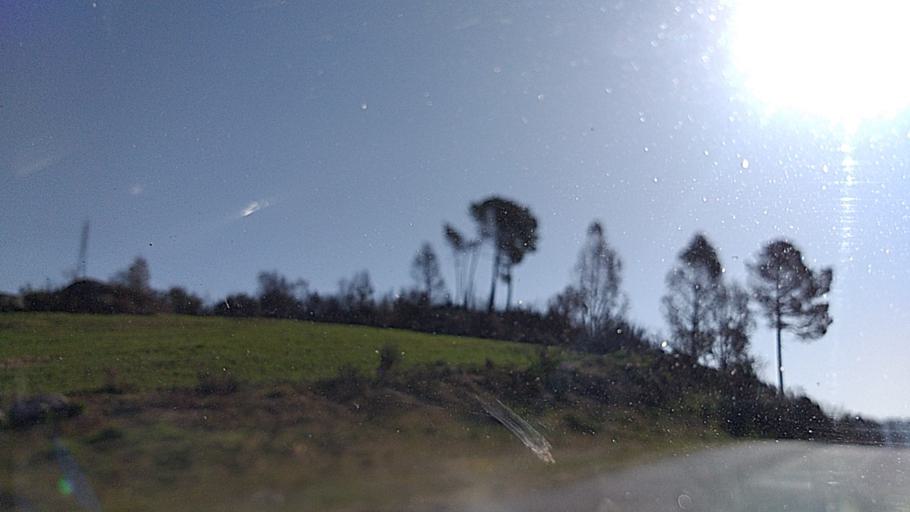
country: PT
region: Guarda
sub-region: Celorico da Beira
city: Celorico da Beira
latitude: 40.6892
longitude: -7.4187
